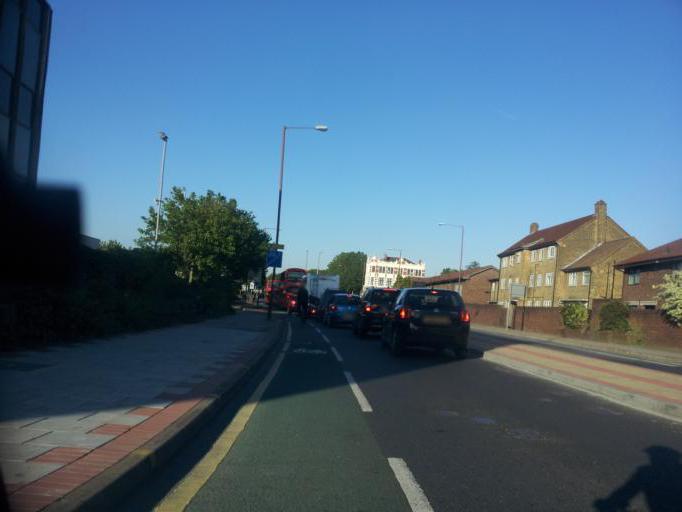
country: GB
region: England
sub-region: Greater London
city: Blackheath
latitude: 51.4876
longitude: 0.0290
